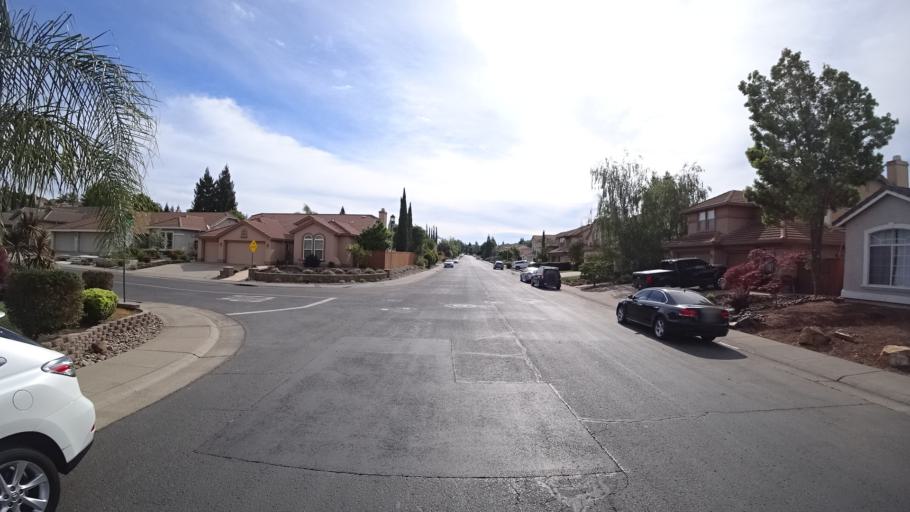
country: US
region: California
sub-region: Placer County
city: Rocklin
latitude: 38.8223
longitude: -121.2801
